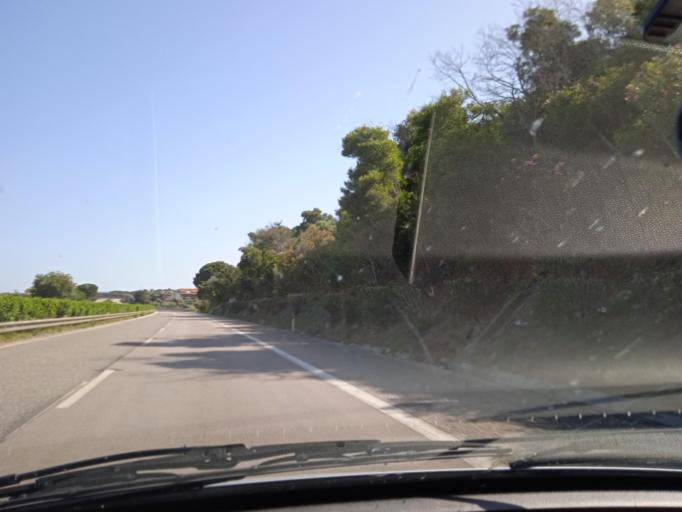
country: IT
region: Sicily
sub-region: Messina
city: Rocca di Capri Leone
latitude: 38.1143
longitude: 14.7250
